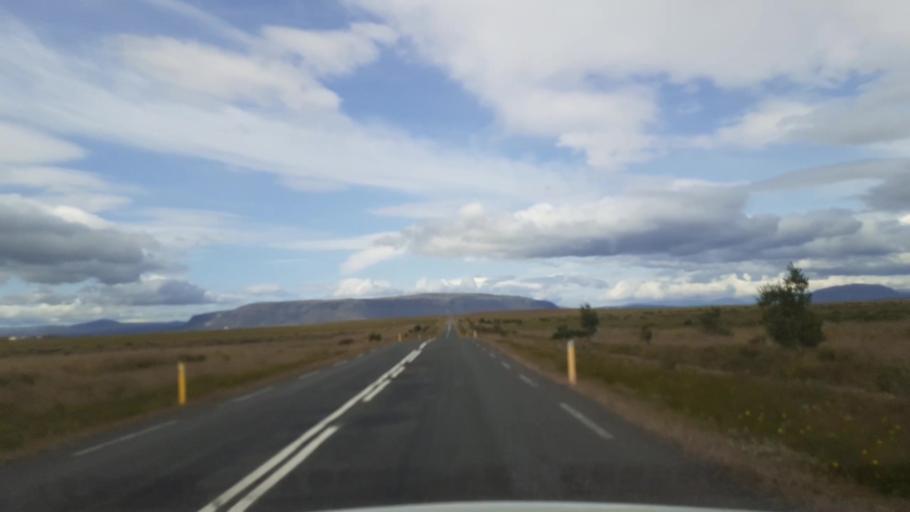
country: IS
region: South
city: Selfoss
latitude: 63.9094
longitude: -20.8262
